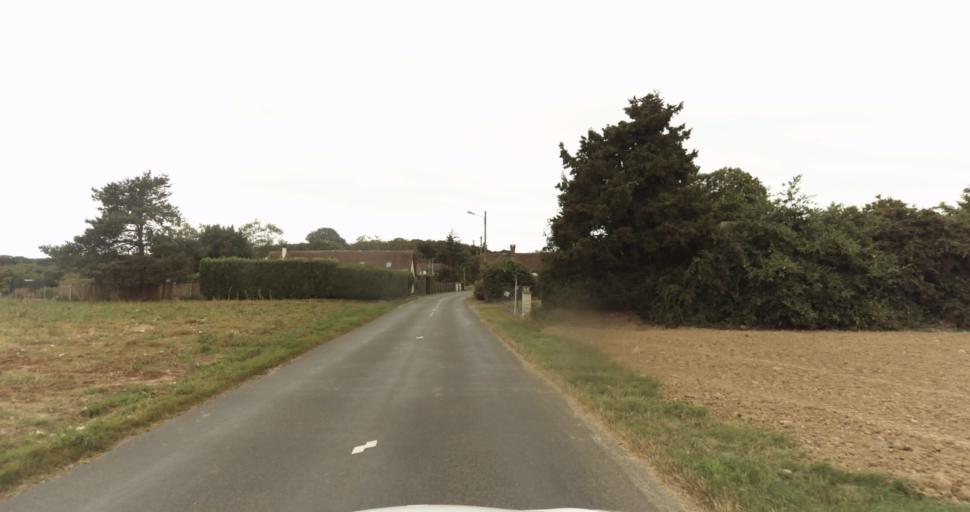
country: FR
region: Haute-Normandie
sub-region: Departement de l'Eure
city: Damville
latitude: 48.9339
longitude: 1.0815
